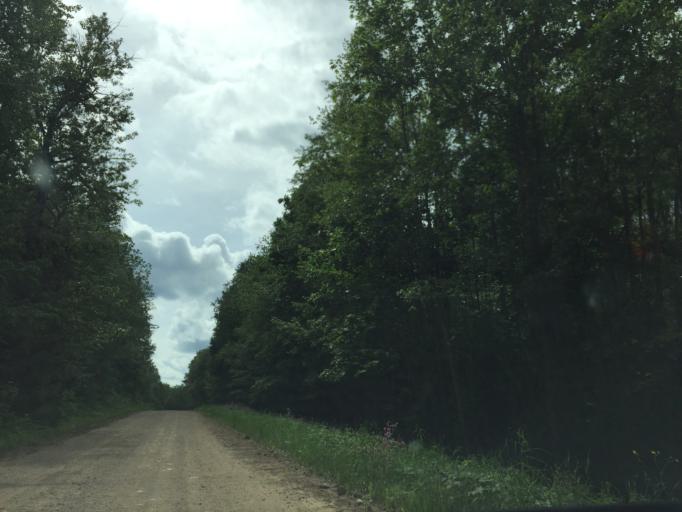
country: LV
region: Dagda
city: Dagda
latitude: 56.0419
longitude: 27.6392
